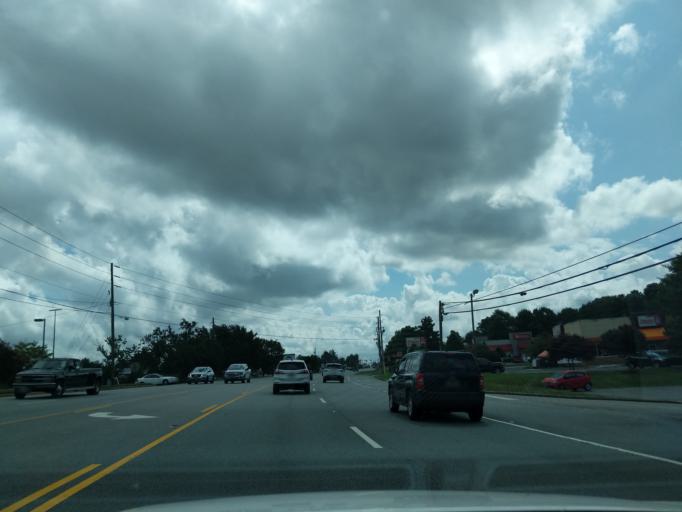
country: US
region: Georgia
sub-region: Columbia County
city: Evans
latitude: 33.5416
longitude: -82.1347
